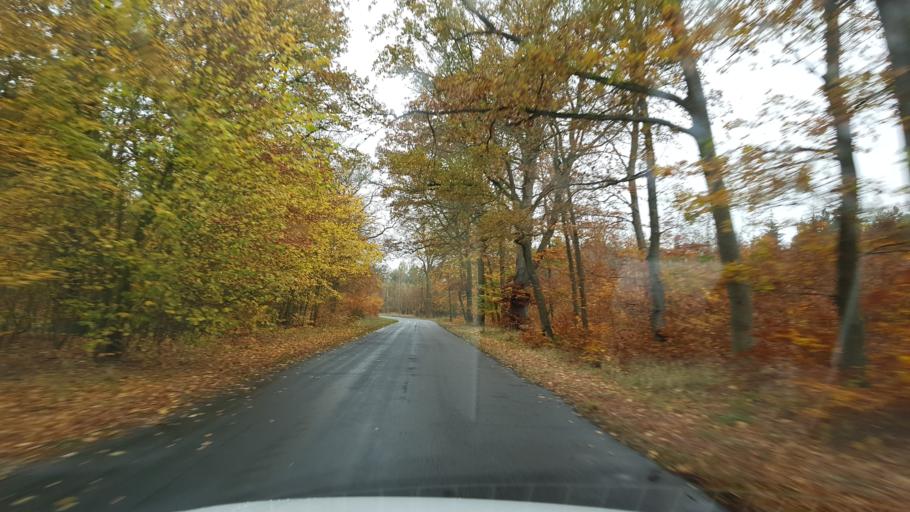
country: PL
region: West Pomeranian Voivodeship
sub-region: Powiat goleniowski
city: Stepnica
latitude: 53.6561
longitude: 14.6679
